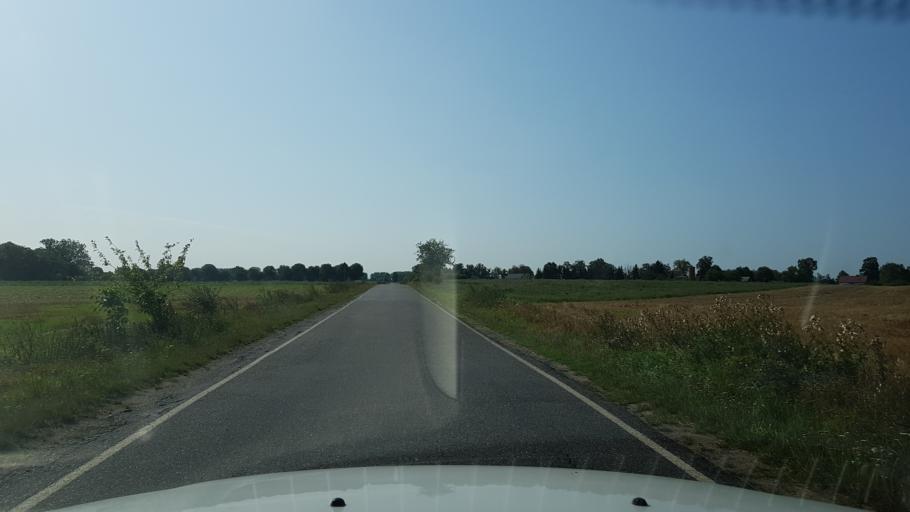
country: PL
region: West Pomeranian Voivodeship
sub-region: Powiat stargardzki
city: Dolice
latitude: 53.1498
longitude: 15.2416
